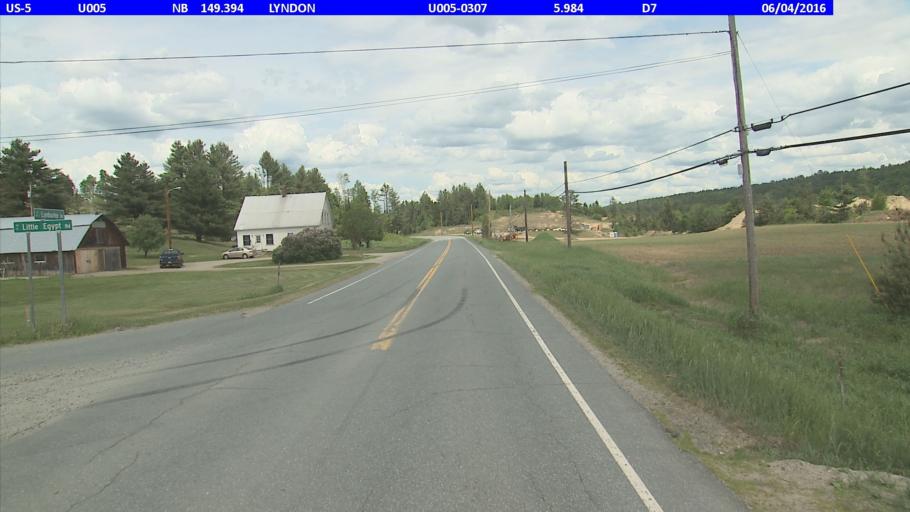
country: US
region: Vermont
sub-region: Caledonia County
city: Lyndonville
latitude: 44.5736
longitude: -71.9872
